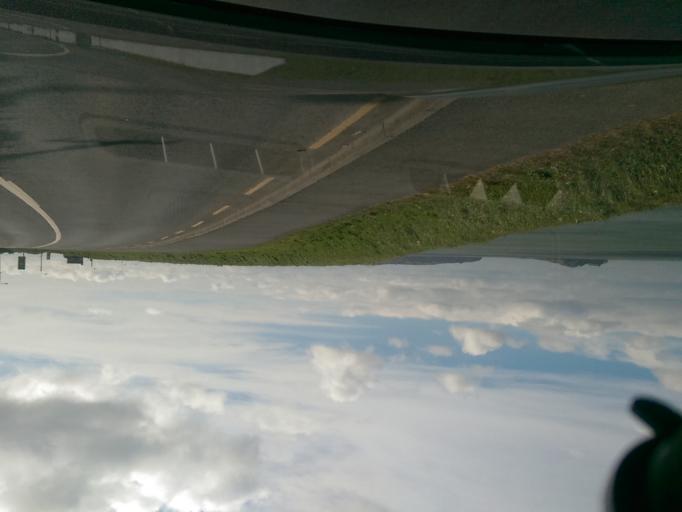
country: IE
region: Leinster
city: Portmarnock
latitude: 53.4396
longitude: -6.1229
